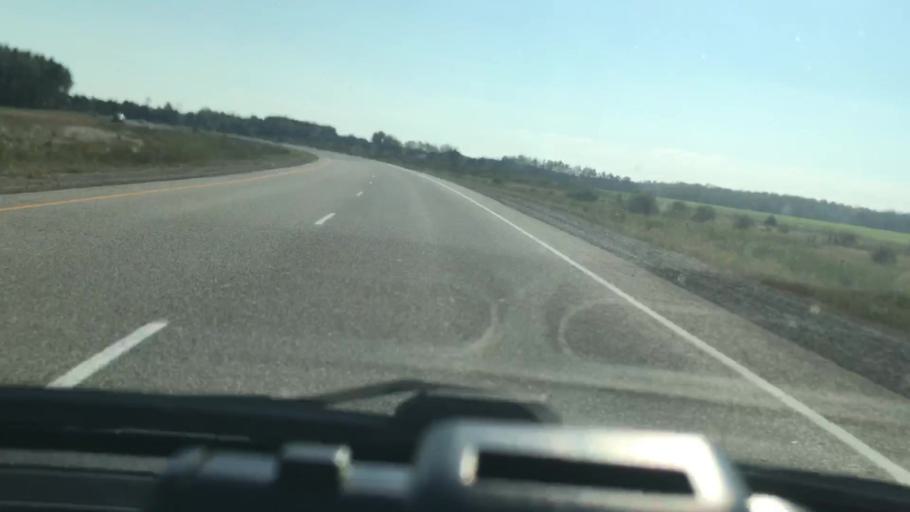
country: CA
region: Ontario
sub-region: Algoma
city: Sault Ste. Marie
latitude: 46.4490
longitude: -84.0658
